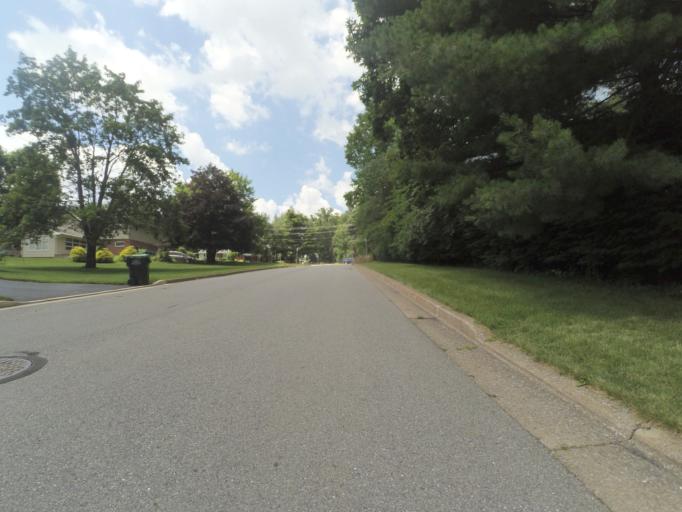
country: US
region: Pennsylvania
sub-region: Centre County
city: State College
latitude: 40.7811
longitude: -77.8437
